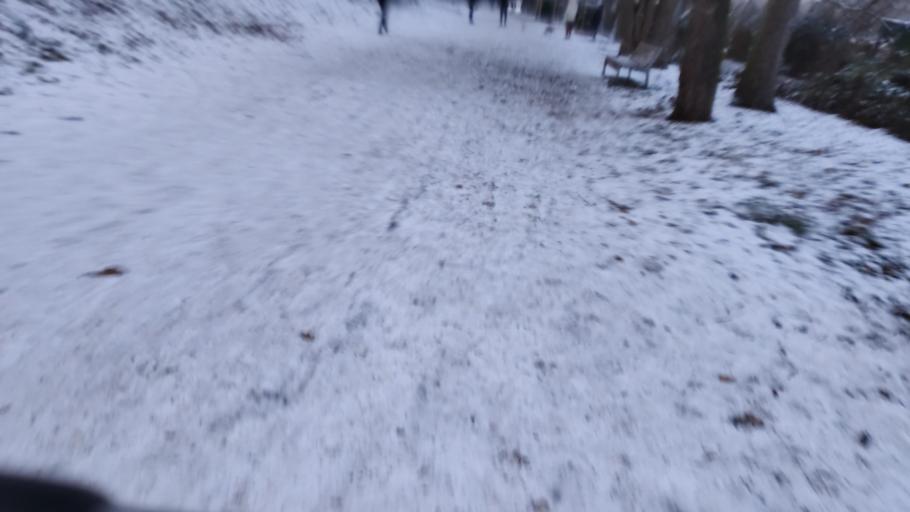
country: PL
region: Lower Silesian Voivodeship
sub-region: Powiat wroclawski
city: Wroclaw
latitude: 51.0819
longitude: 16.9977
